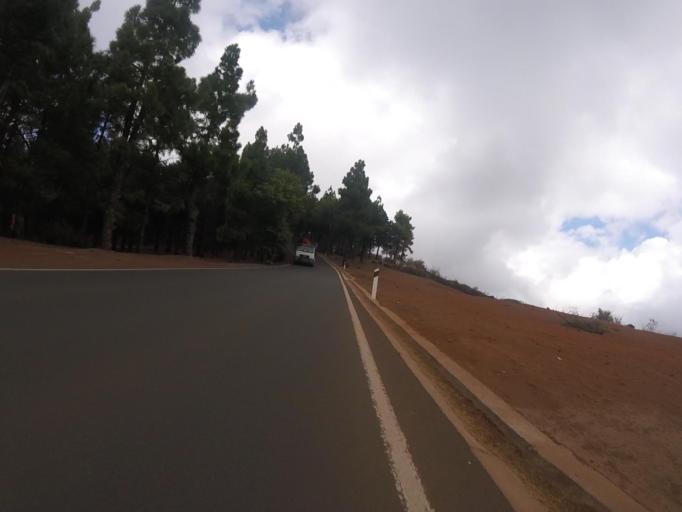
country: ES
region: Canary Islands
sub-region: Provincia de Las Palmas
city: San Bartolome
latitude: 27.9722
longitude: -15.5734
